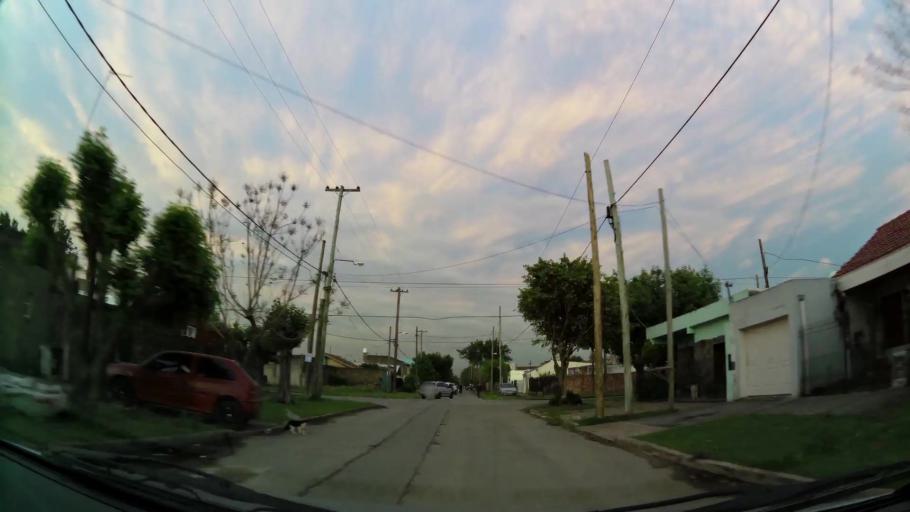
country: AR
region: Buenos Aires
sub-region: Partido de Lomas de Zamora
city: Lomas de Zamora
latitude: -34.7544
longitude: -58.3617
